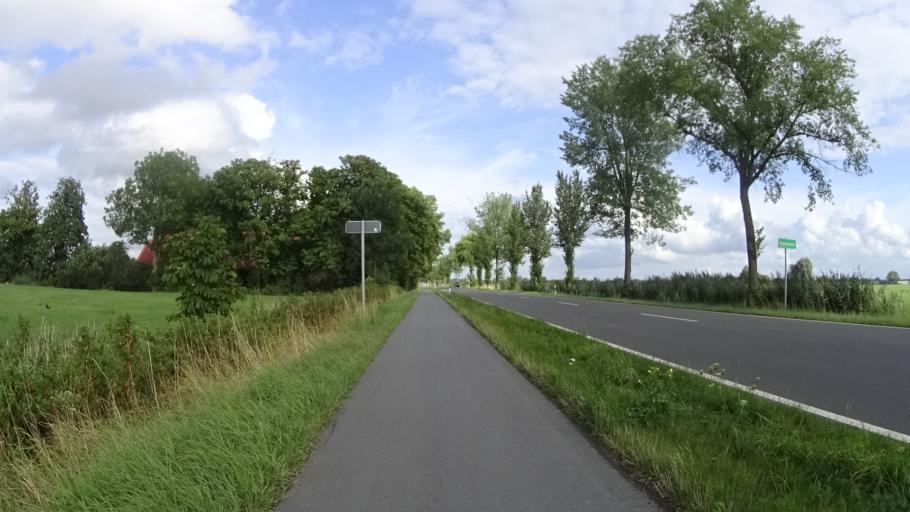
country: DE
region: Lower Saxony
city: Varel
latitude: 53.3869
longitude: 8.2091
